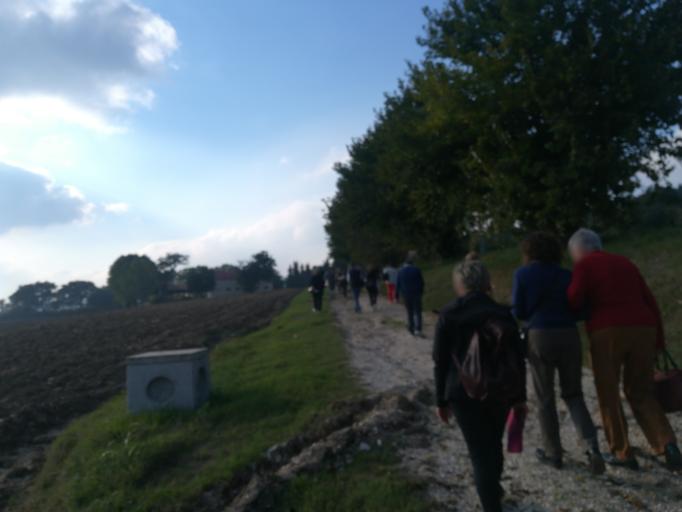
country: IT
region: The Marches
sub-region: Provincia di Macerata
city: Sforzacosta
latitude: 43.2705
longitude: 13.4292
